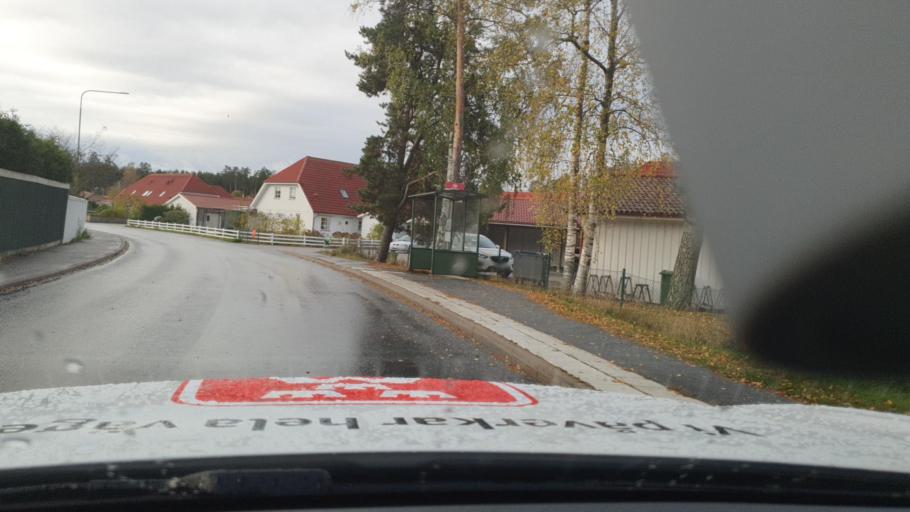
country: SE
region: Stockholm
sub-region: Vallentuna Kommun
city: Vallentuna
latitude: 59.4996
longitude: 18.0825
